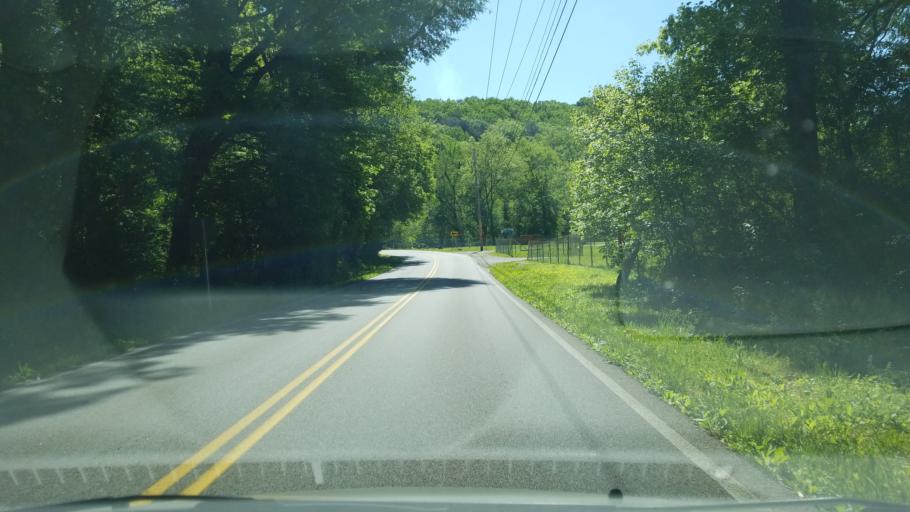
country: US
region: Tennessee
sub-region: Hamilton County
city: Falling Water
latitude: 35.1751
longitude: -85.2295
